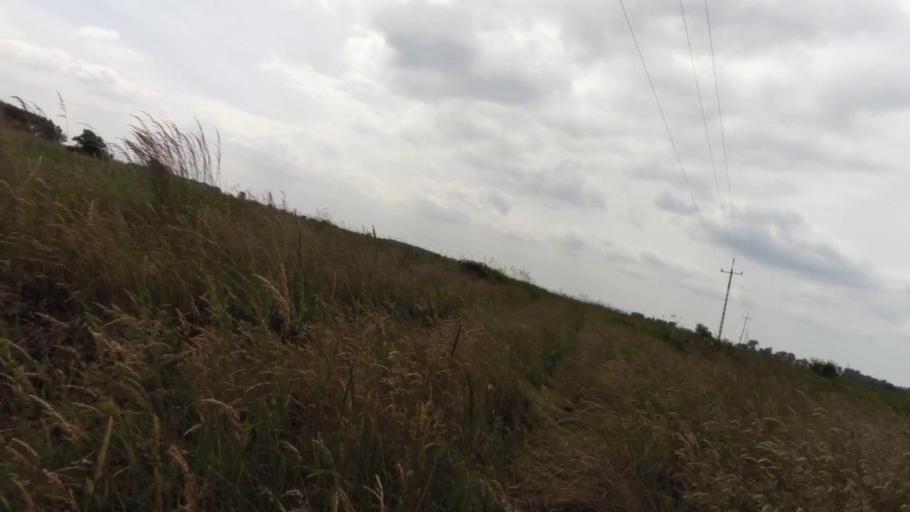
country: PL
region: West Pomeranian Voivodeship
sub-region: Powiat goleniowski
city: Goleniow
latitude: 53.4971
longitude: 14.7056
